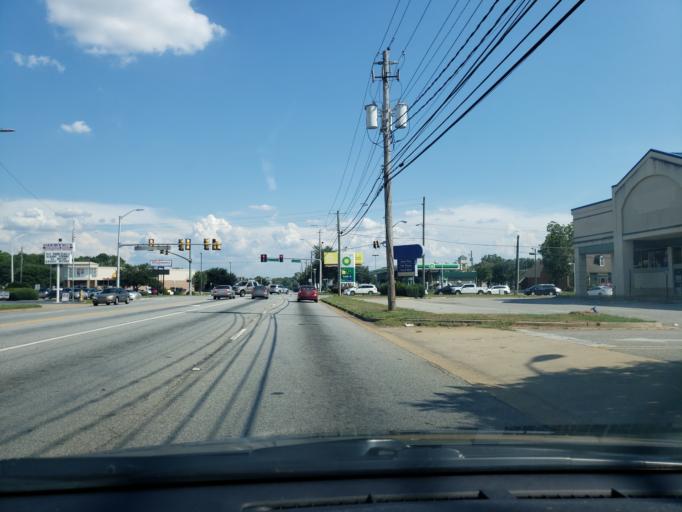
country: US
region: Georgia
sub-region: Dougherty County
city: Albany
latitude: 31.6065
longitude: -84.2076
